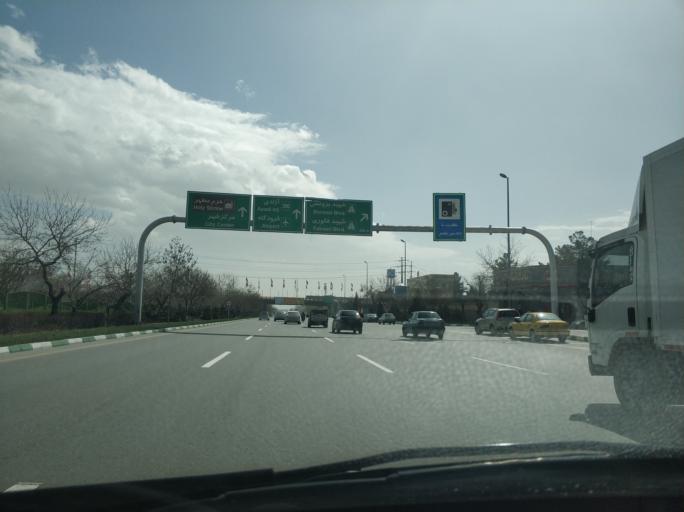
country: IR
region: Razavi Khorasan
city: Torqabeh
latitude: 36.3407
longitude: 59.4582
